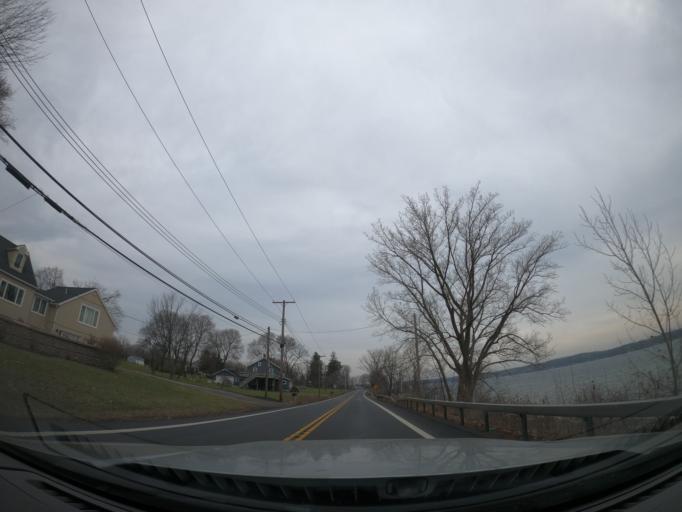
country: US
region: New York
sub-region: Cayuga County
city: Melrose Park
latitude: 42.8570
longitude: -76.5316
